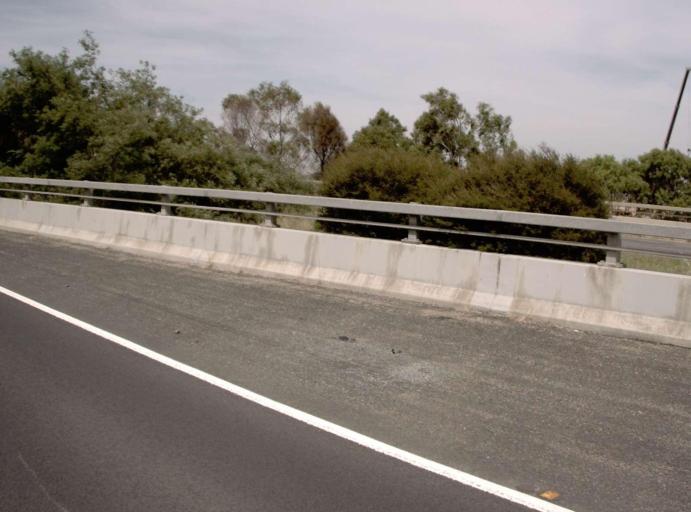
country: AU
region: Victoria
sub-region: Casey
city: Lynbrook
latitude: -38.0484
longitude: 145.2453
